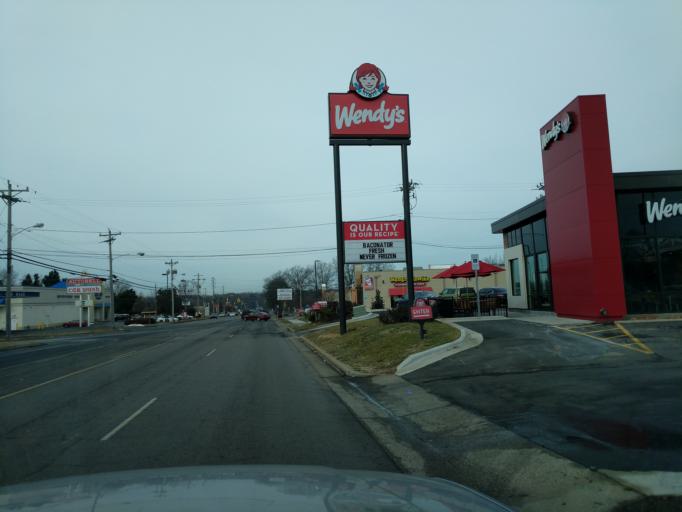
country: US
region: North Carolina
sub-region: Iredell County
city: Statesville
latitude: 35.7905
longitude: -80.8544
